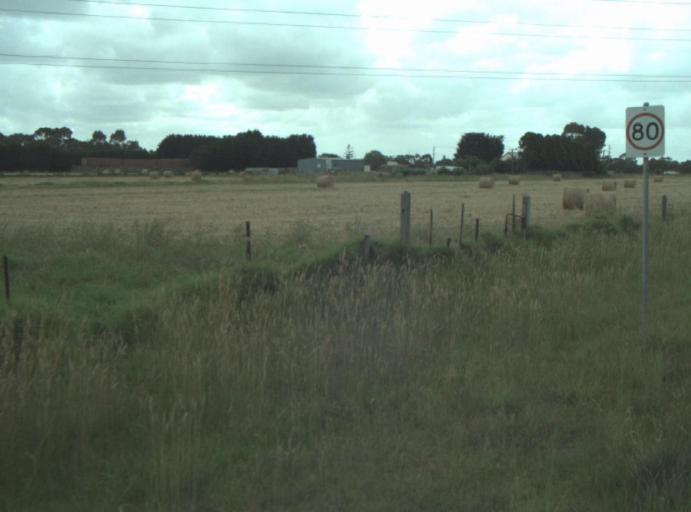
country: AU
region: Victoria
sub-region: Greater Geelong
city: Leopold
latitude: -38.1810
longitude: 144.4198
